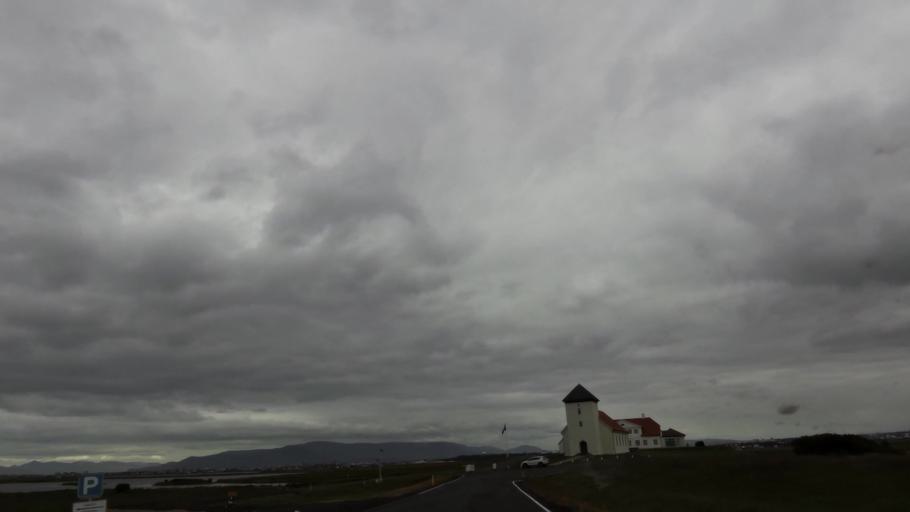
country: IS
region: Capital Region
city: Alftanes
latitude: 64.1054
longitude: -21.9990
